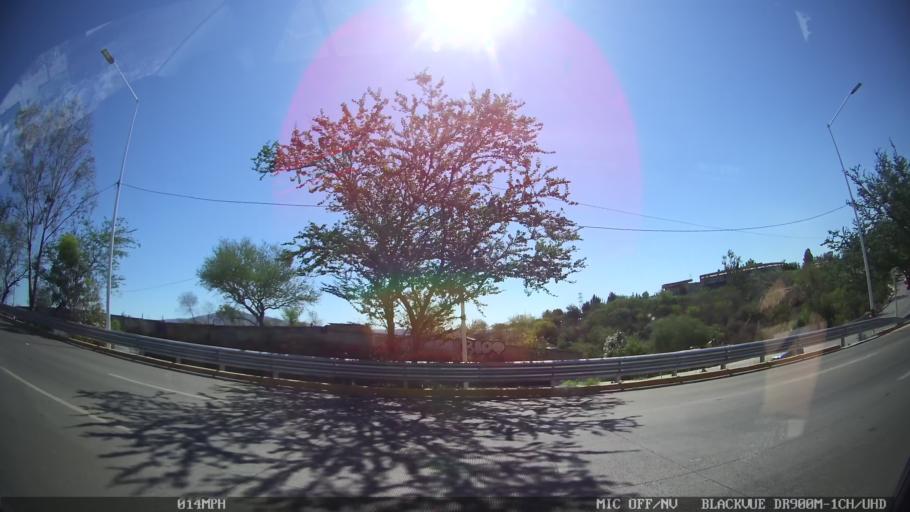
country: MX
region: Jalisco
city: Tlaquepaque
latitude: 20.7052
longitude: -103.2864
